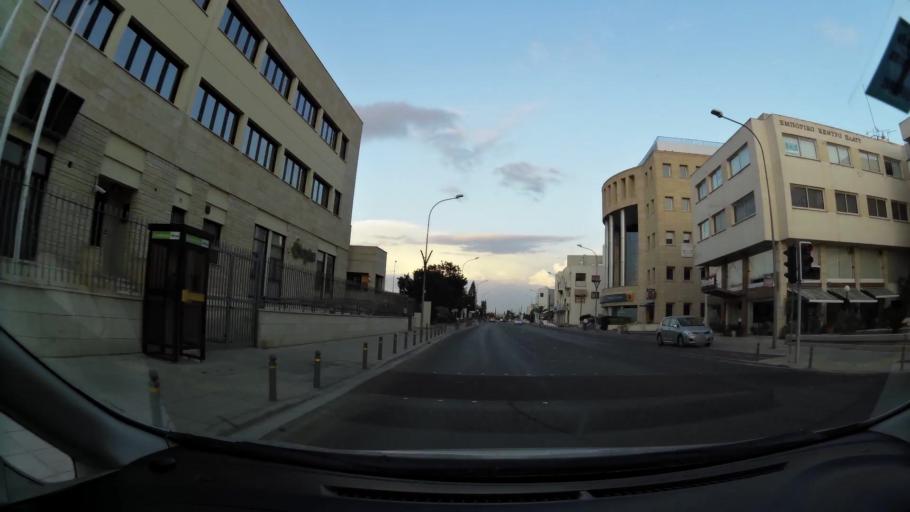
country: CY
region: Lefkosia
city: Nicosia
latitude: 35.1493
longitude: 33.3922
